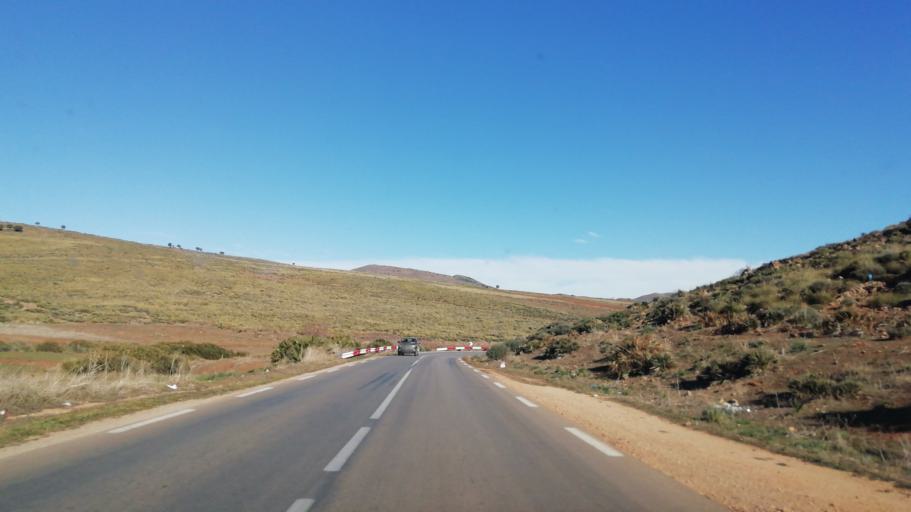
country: DZ
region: Tlemcen
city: Ouled Mimoun
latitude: 34.7705
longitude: -1.1362
